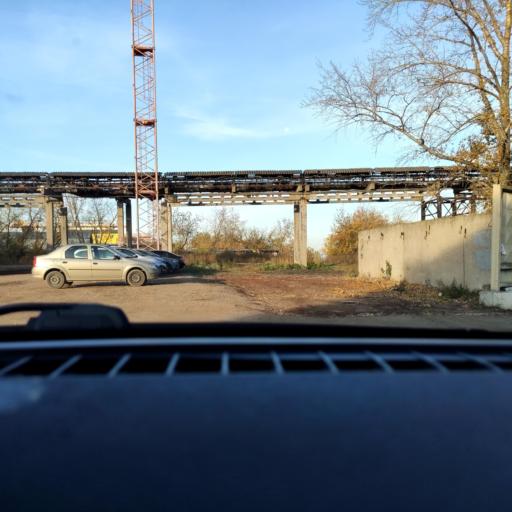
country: RU
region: Perm
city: Perm
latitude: 58.0128
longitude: 56.1812
